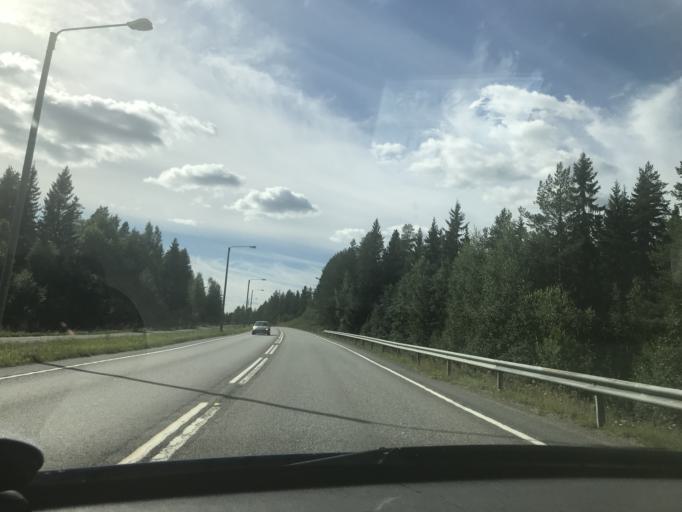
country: FI
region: Southern Ostrobothnia
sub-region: Kuusiokunnat
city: Alavus
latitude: 62.5968
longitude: 23.6591
